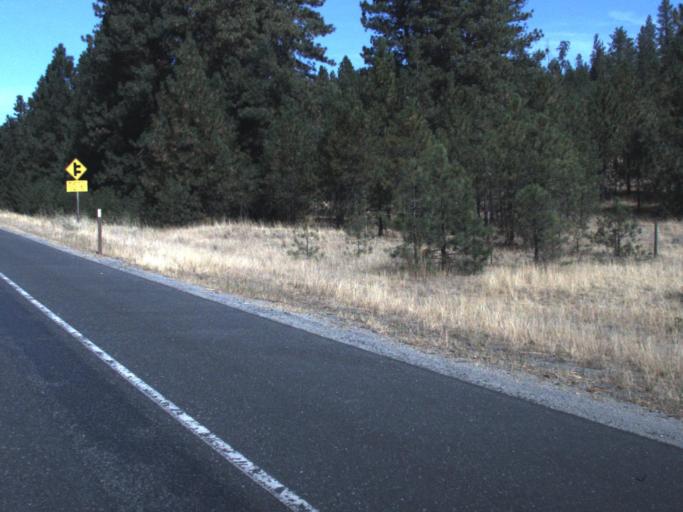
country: US
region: Washington
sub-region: Stevens County
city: Colville
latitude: 48.3957
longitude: -117.8478
